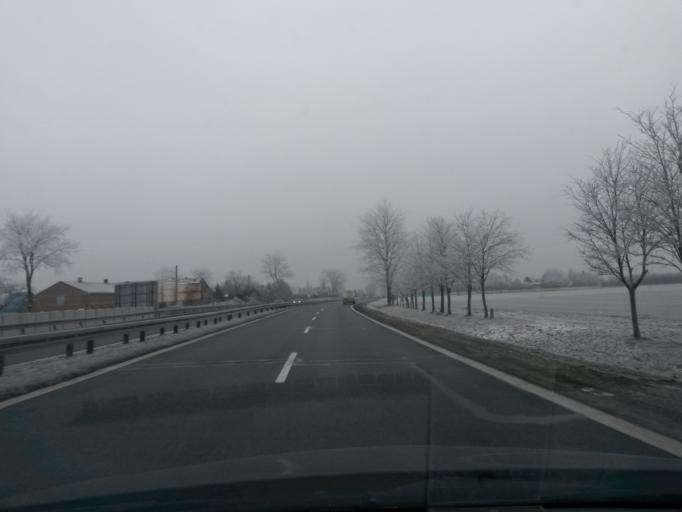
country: PL
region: Greater Poland Voivodeship
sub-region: Powiat poznanski
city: Kostrzyn
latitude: 52.3968
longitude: 17.1893
